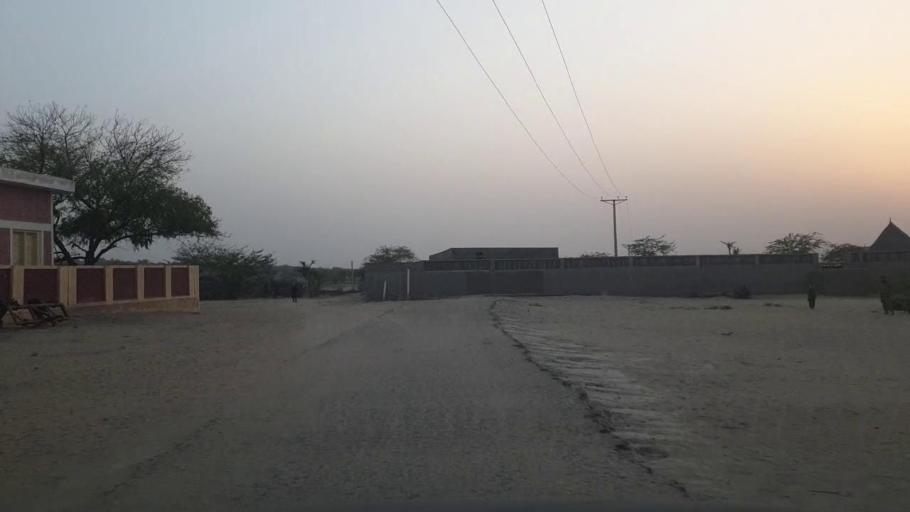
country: PK
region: Sindh
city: Chor
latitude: 25.4987
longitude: 69.8232
